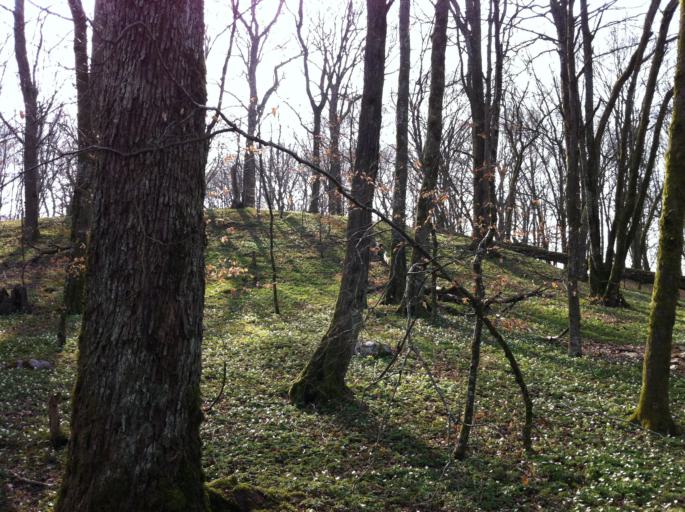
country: SE
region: Skane
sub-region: Eslovs Kommun
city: Stehag
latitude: 56.0114
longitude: 13.3892
